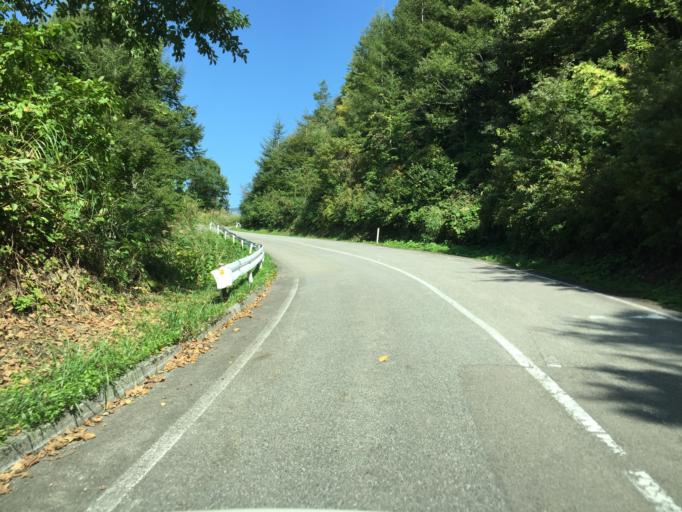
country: JP
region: Fukushima
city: Inawashiro
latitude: 37.6728
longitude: 140.1131
